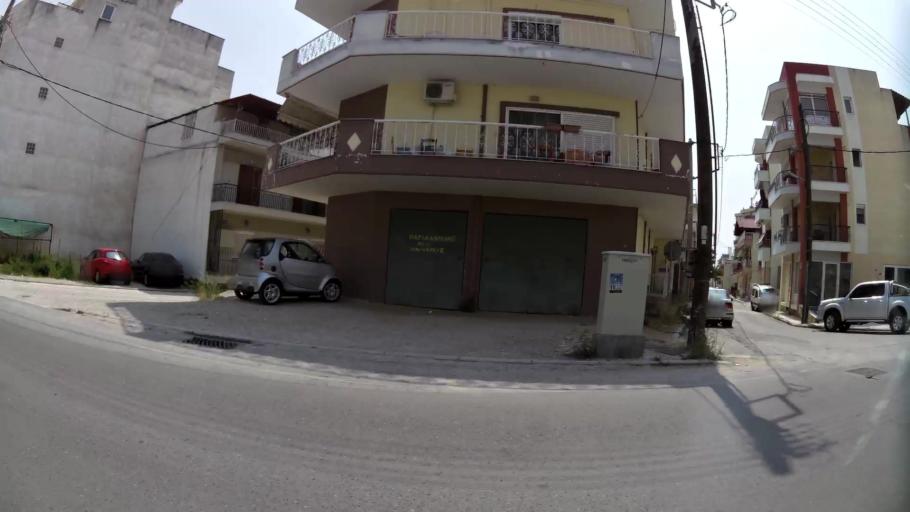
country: GR
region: Central Macedonia
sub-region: Nomos Thessalonikis
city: Evosmos
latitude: 40.6636
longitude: 22.9068
